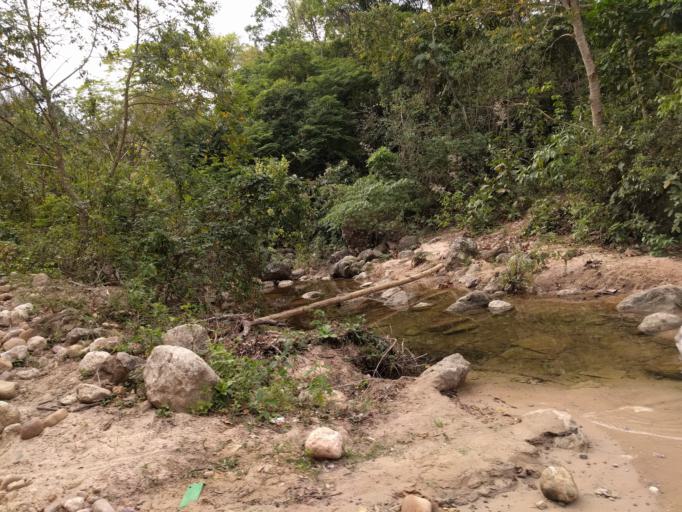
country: BO
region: Santa Cruz
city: Santiago del Torno
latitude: -17.9092
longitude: -63.4363
